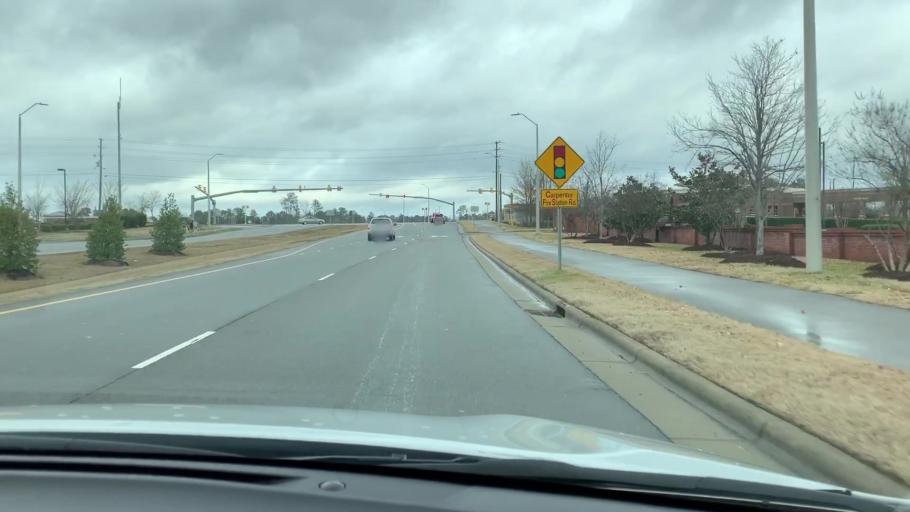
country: US
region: North Carolina
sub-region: Wake County
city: Green Level
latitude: 35.8210
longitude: -78.9023
